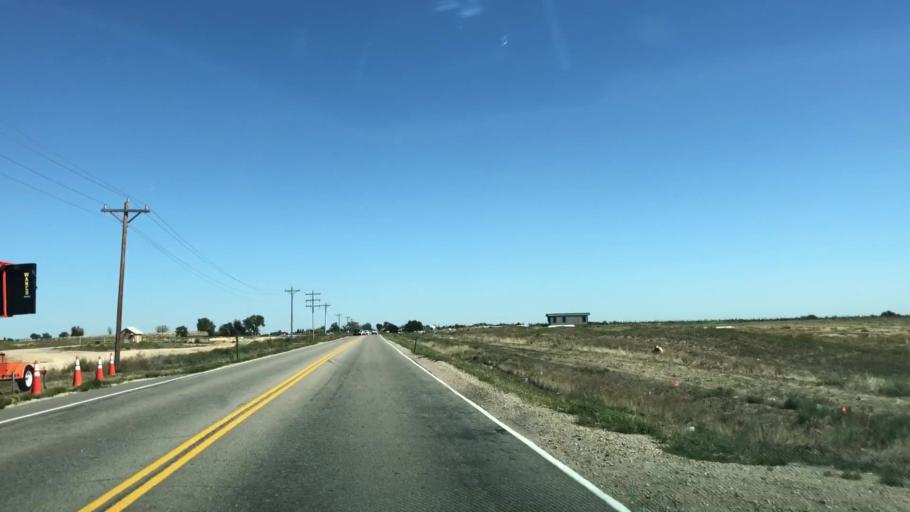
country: US
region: Colorado
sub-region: Weld County
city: Windsor
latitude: 40.5228
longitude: -104.9419
